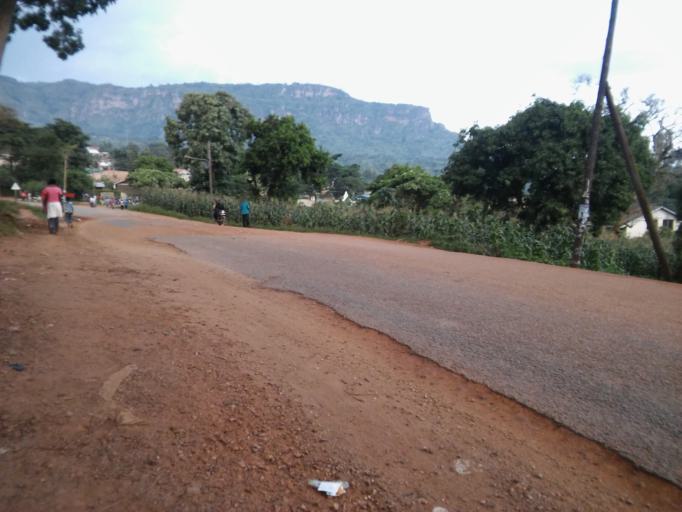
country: UG
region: Eastern Region
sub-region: Mbale District
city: Mbale
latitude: 1.0634
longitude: 34.1997
